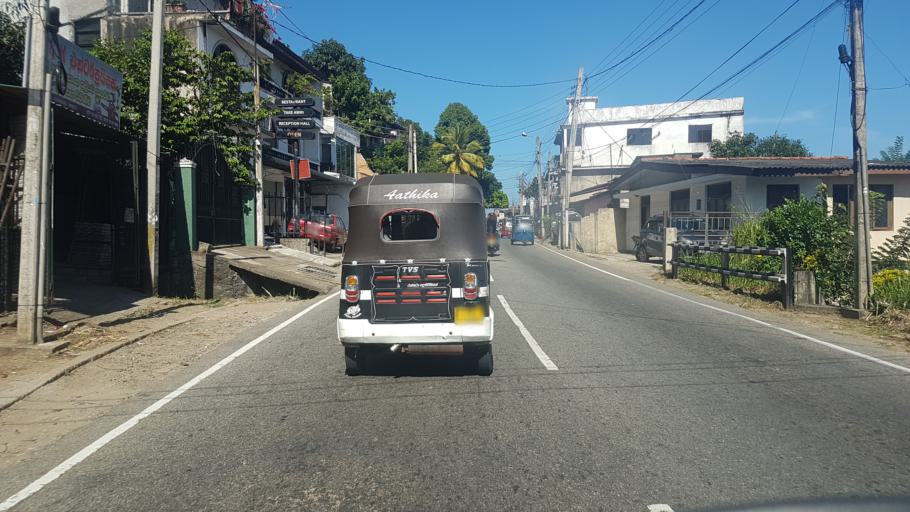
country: LK
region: Central
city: Kandy
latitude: 7.2880
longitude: 80.6577
